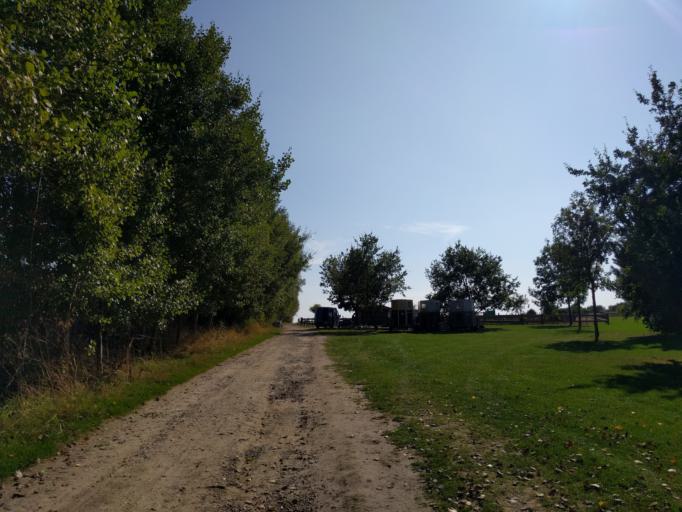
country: DE
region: Schleswig-Holstein
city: Fehmarn
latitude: 54.4040
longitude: 11.1740
